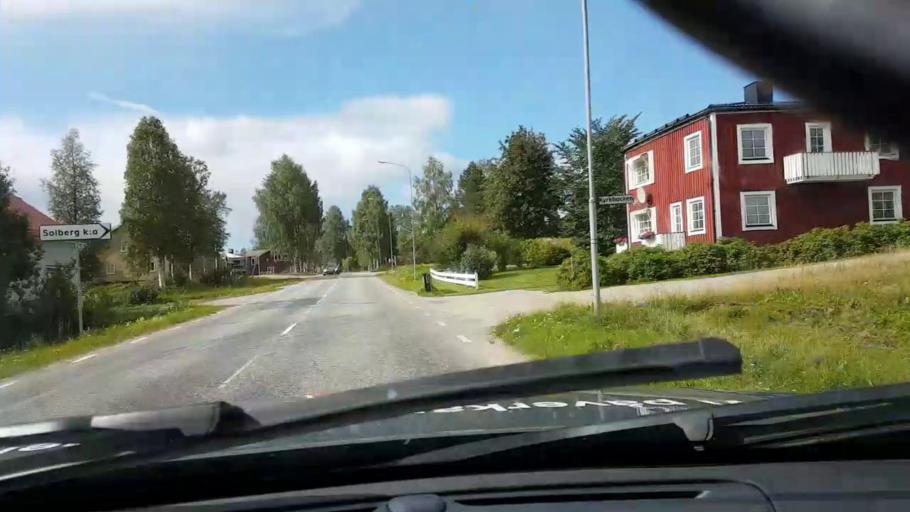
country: SE
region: Vaesterbotten
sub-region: Asele Kommun
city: Asele
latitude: 63.7902
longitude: 17.6344
